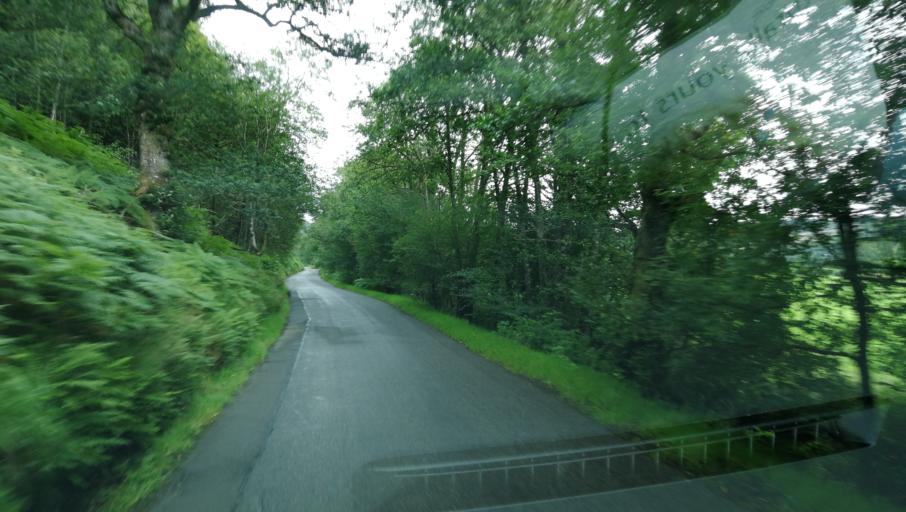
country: GB
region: Scotland
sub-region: Highland
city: Beauly
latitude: 57.3358
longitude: -4.7830
